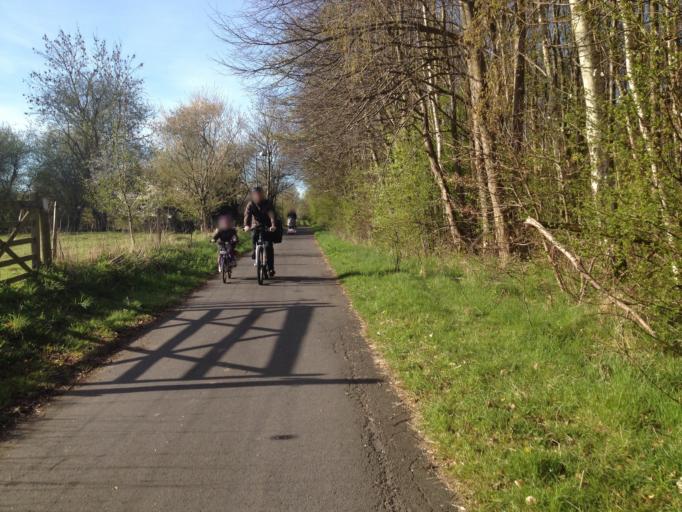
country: DK
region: Capital Region
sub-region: Ballerup Kommune
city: Ballerup
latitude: 55.7439
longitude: 12.3766
